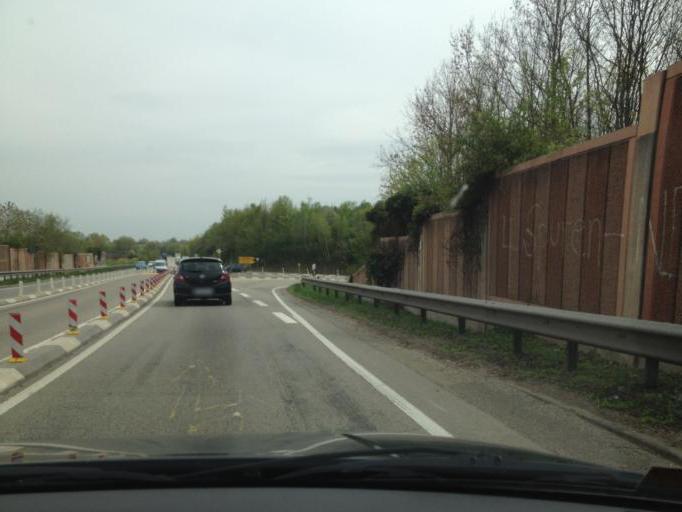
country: DE
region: Rheinland-Pfalz
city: Birkweiler
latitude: 49.2072
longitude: 8.0423
